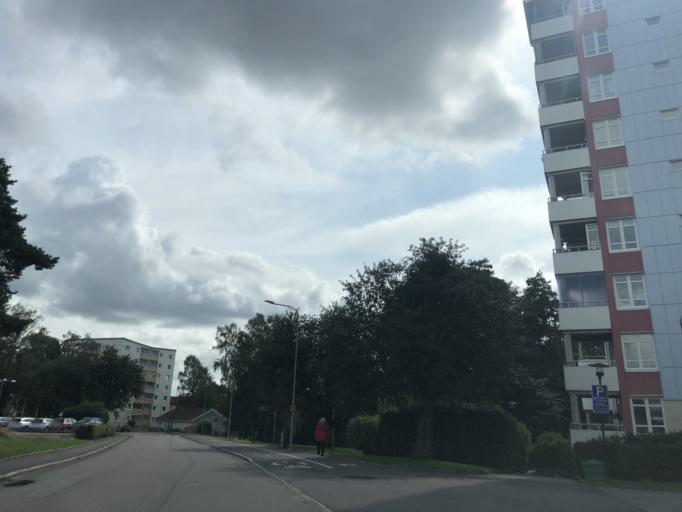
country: SE
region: Vaestra Goetaland
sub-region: Goteborg
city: Majorna
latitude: 57.7169
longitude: 11.8869
